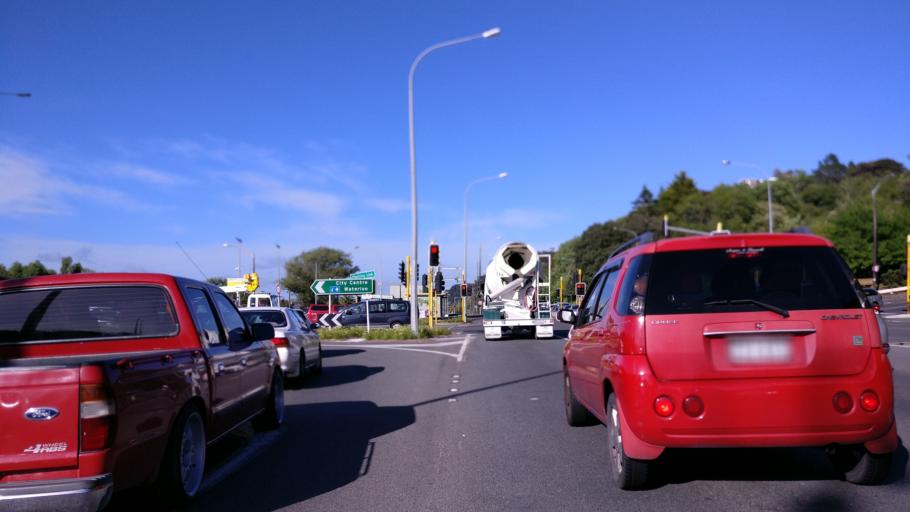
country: NZ
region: Wellington
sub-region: Lower Hutt City
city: Lower Hutt
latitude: -41.2030
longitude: 174.9065
